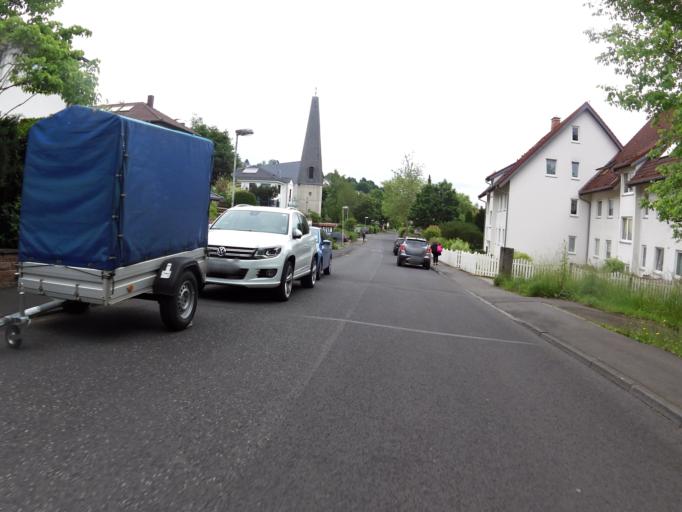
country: DE
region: Hesse
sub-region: Regierungsbezirk Kassel
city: Bad Hersfeld
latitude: 50.8704
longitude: 9.6852
